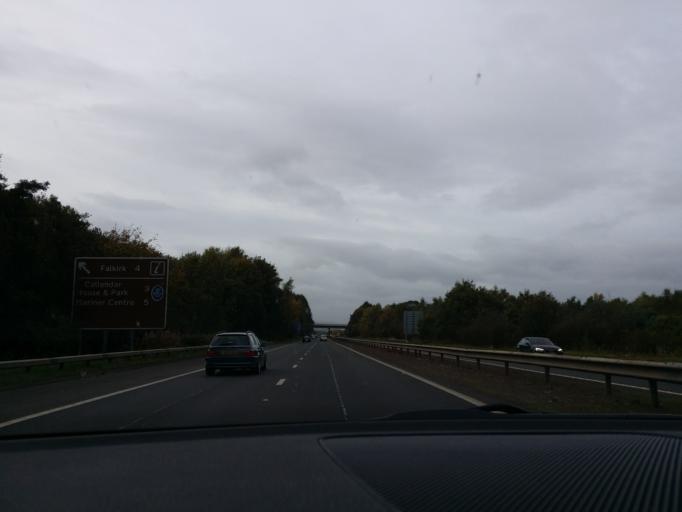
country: GB
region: Scotland
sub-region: Falkirk
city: Polmont
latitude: 55.9919
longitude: -3.7006
